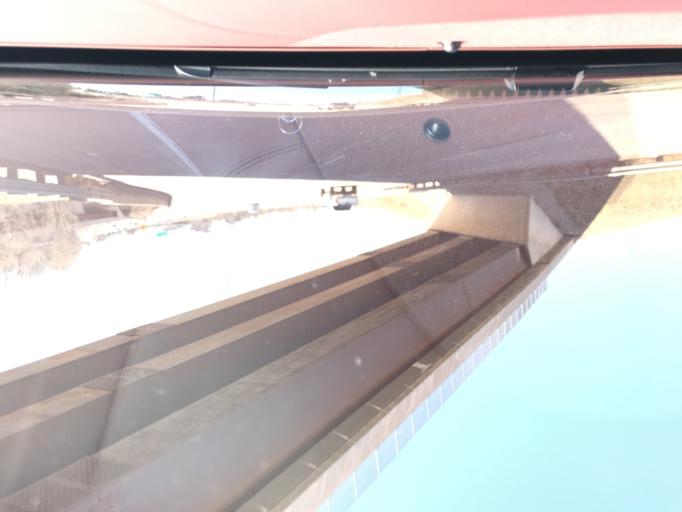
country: US
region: Colorado
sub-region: Jefferson County
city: Arvada
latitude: 39.7863
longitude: -105.0762
